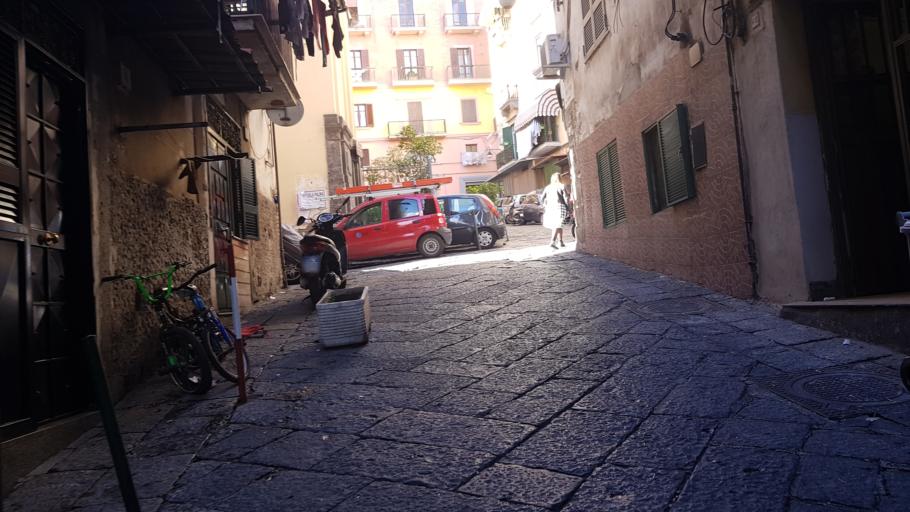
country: IT
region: Campania
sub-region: Provincia di Napoli
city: Napoli
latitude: 40.8396
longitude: 14.2451
